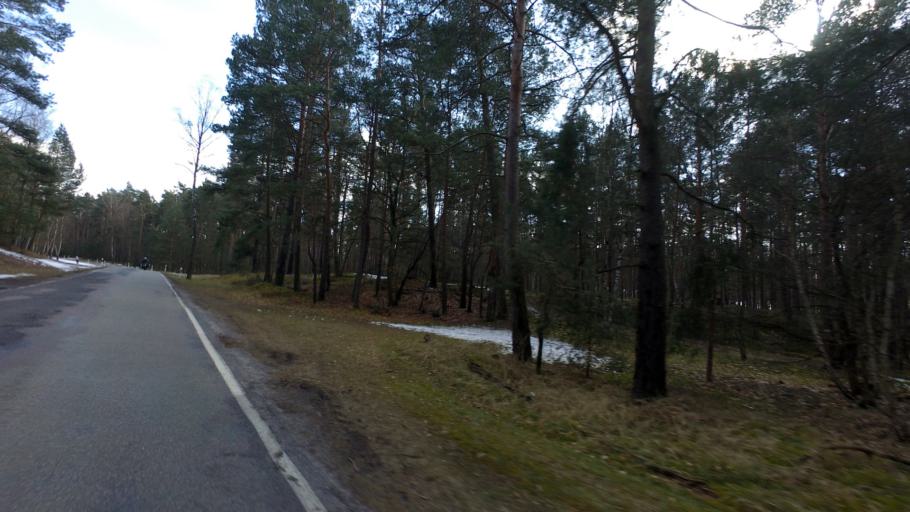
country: DE
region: Brandenburg
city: Marienwerder
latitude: 52.8008
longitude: 13.5917
